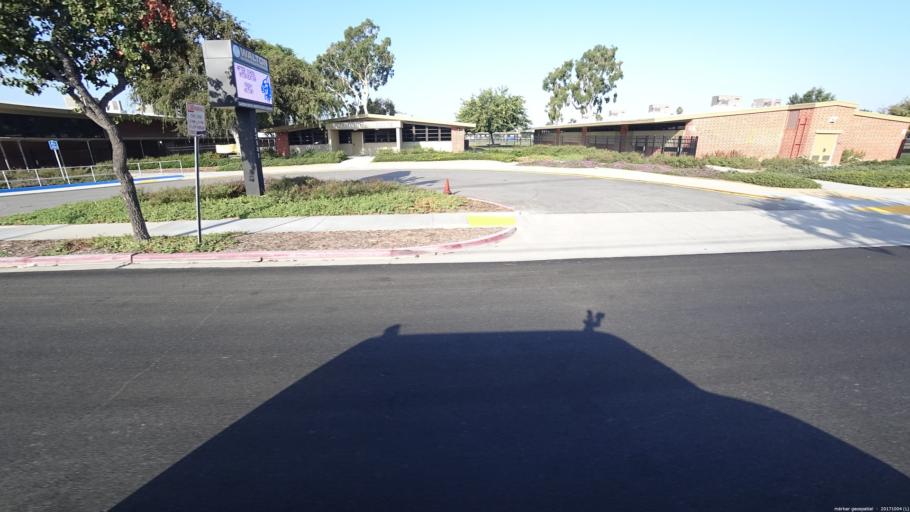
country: US
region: California
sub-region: Orange County
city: Garden Grove
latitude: 33.7860
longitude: -117.9192
